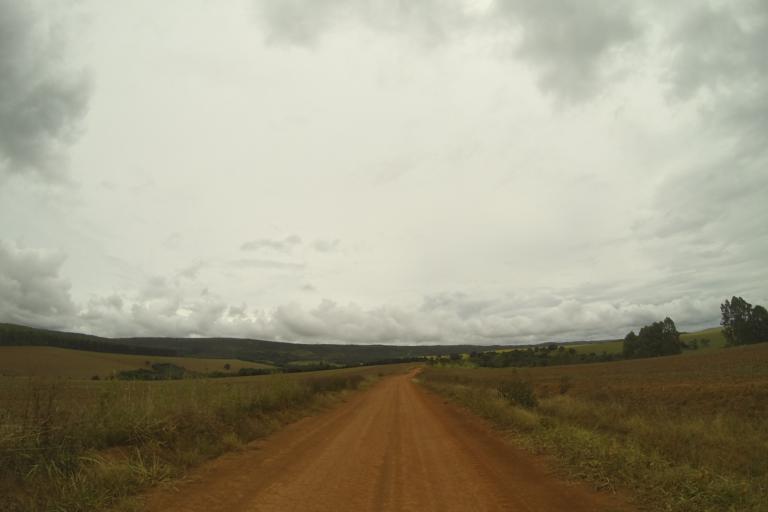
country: BR
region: Minas Gerais
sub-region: Ibia
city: Ibia
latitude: -19.7416
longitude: -46.6136
